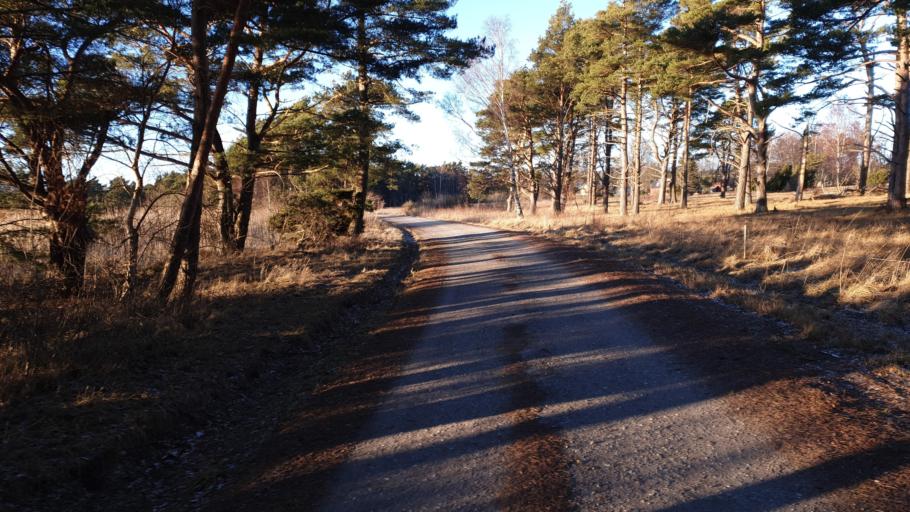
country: SE
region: Gotland
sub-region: Gotland
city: Slite
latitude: 57.3735
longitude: 18.8049
